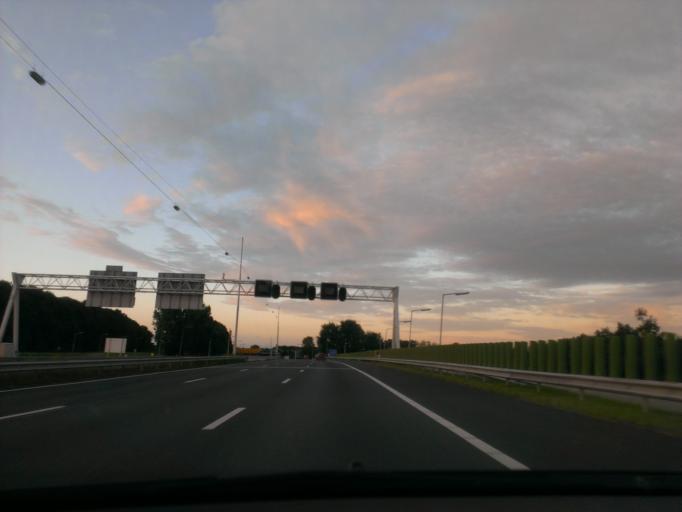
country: NL
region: South Holland
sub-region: Gemeente Binnenmaas
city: Heinenoord
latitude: 51.8257
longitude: 4.5058
